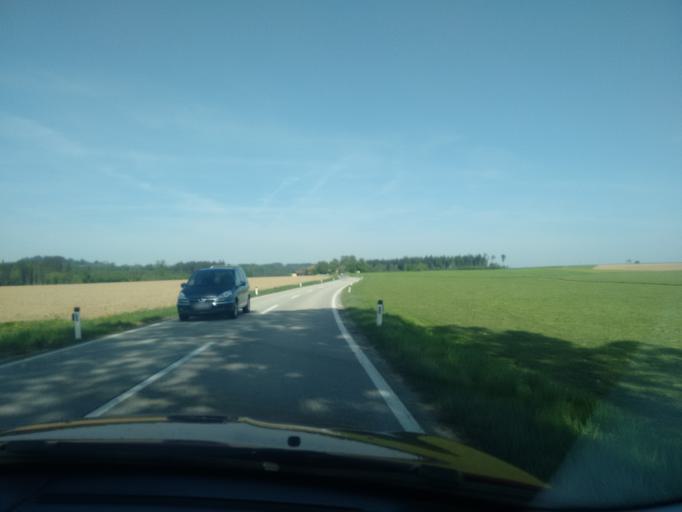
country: AT
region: Upper Austria
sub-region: Politischer Bezirk Grieskirchen
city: Grieskirchen
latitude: 48.3353
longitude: 13.8257
